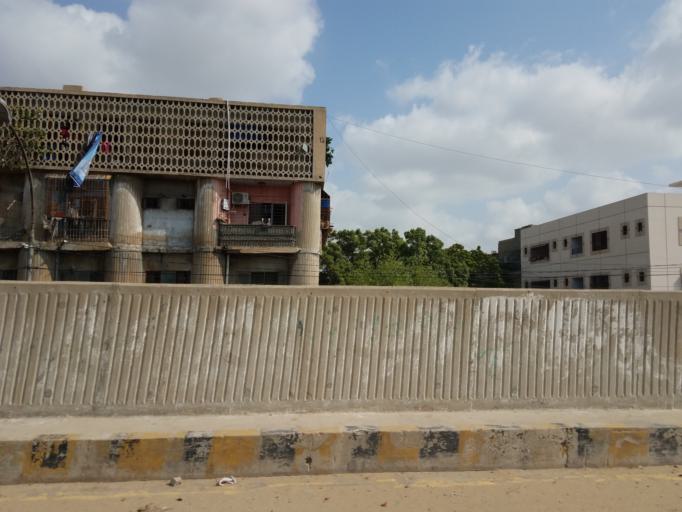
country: PK
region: Sindh
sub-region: Karachi District
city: Karachi
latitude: 24.9174
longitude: 67.0528
